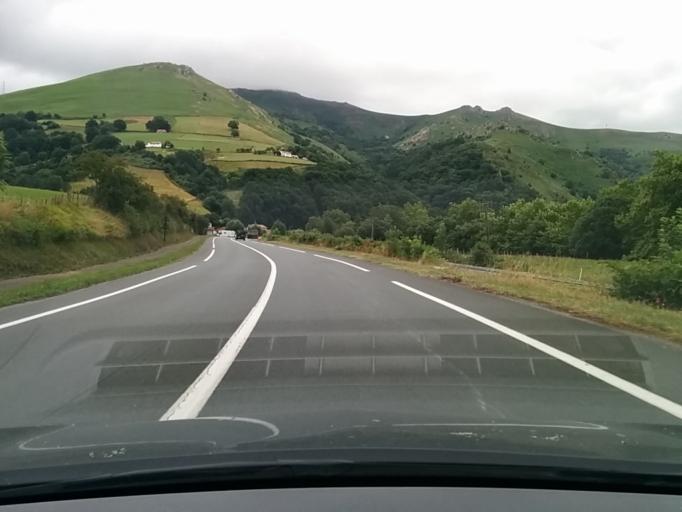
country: FR
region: Aquitaine
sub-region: Departement des Pyrenees-Atlantiques
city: Saint-Etienne-de-Baigorry
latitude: 43.2661
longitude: -1.3368
